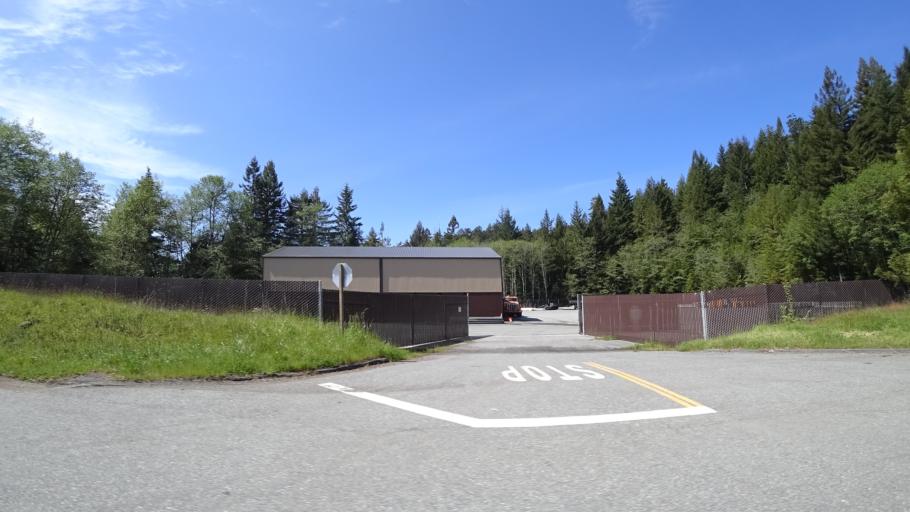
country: US
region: California
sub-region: Humboldt County
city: Westhaven-Moonstone
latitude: 41.4076
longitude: -124.0026
